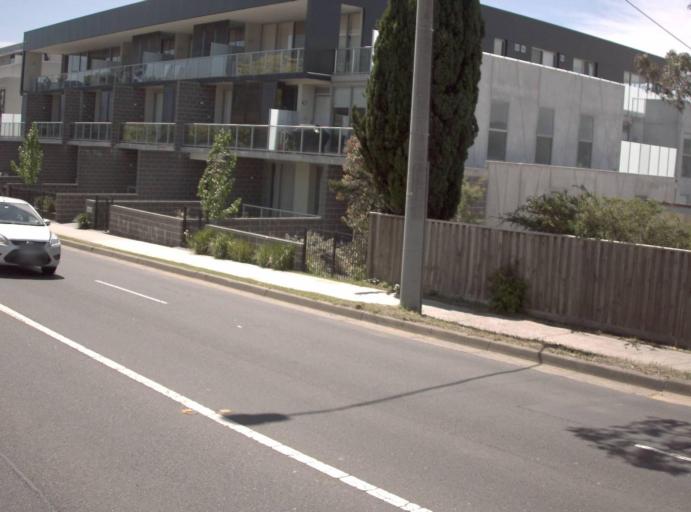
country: AU
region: Victoria
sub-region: Monash
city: Notting Hill
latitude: -37.8777
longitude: 145.1473
